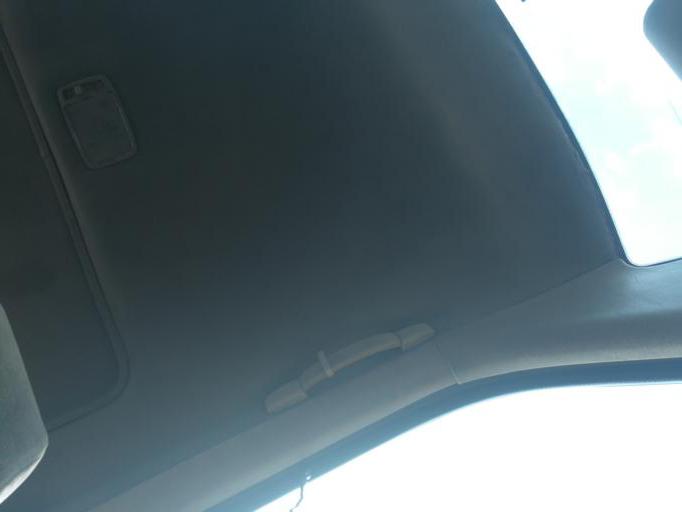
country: NG
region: Lagos
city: Ikorodu
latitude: 6.6429
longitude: 3.5537
